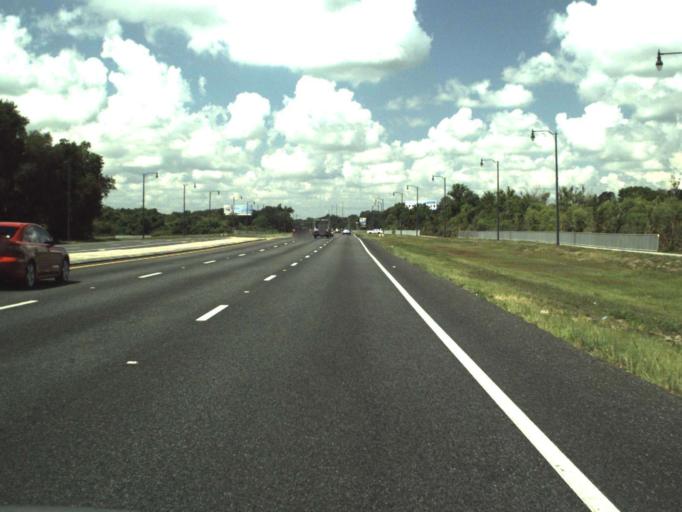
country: US
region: Florida
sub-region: Lake County
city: Silver Lake
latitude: 28.8293
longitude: -81.8247
